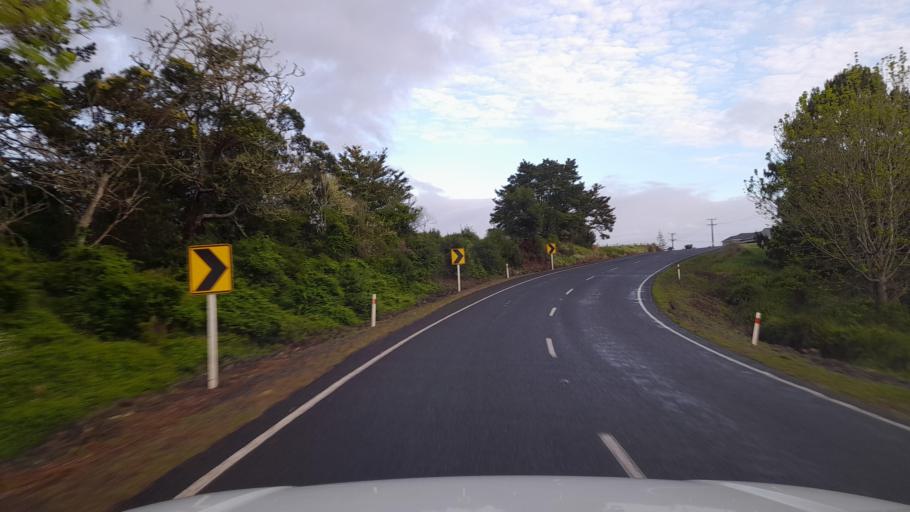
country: NZ
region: Northland
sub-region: Kaipara District
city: Dargaville
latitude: -35.6901
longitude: 173.9007
